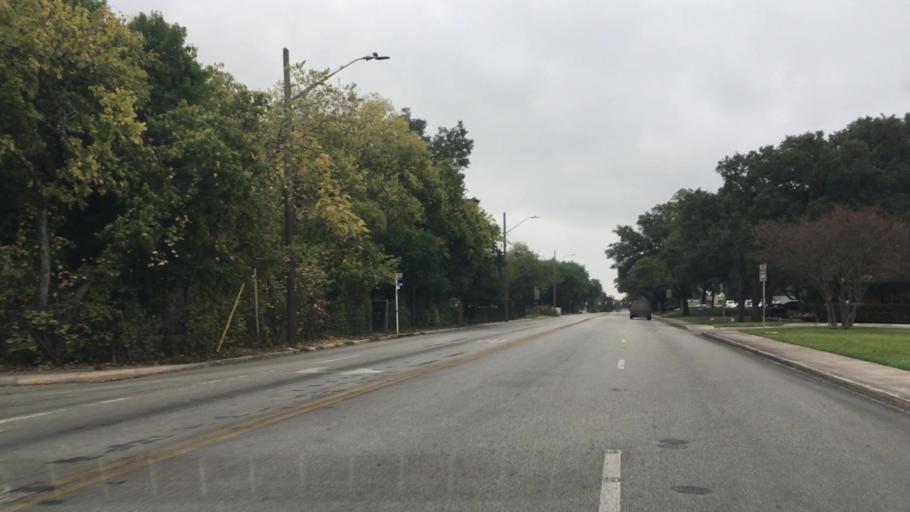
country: US
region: Texas
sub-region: Bexar County
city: Balcones Heights
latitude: 29.4765
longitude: -98.5478
